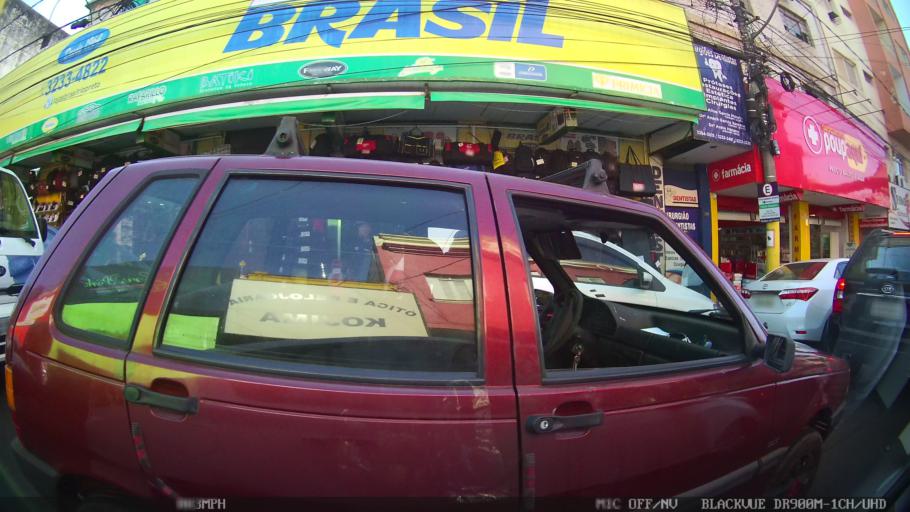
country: BR
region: Sao Paulo
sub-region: Sao Jose Do Rio Preto
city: Sao Jose do Rio Preto
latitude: -20.8089
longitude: -49.3782
